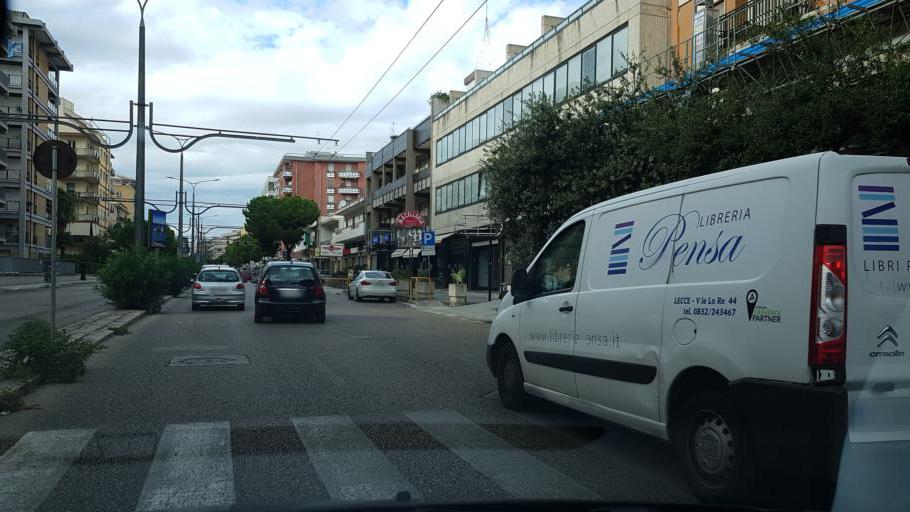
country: IT
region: Apulia
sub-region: Provincia di Lecce
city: Lecce
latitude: 40.3538
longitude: 18.1856
